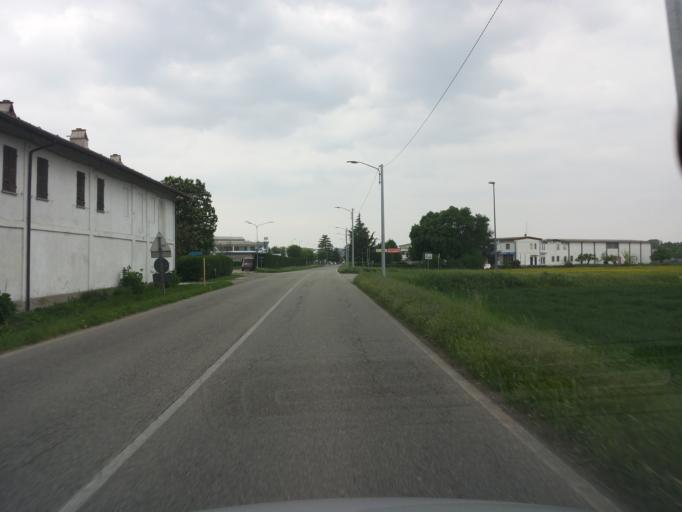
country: IT
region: Piedmont
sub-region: Provincia di Alessandria
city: Occimiano
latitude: 45.0669
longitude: 8.4976
